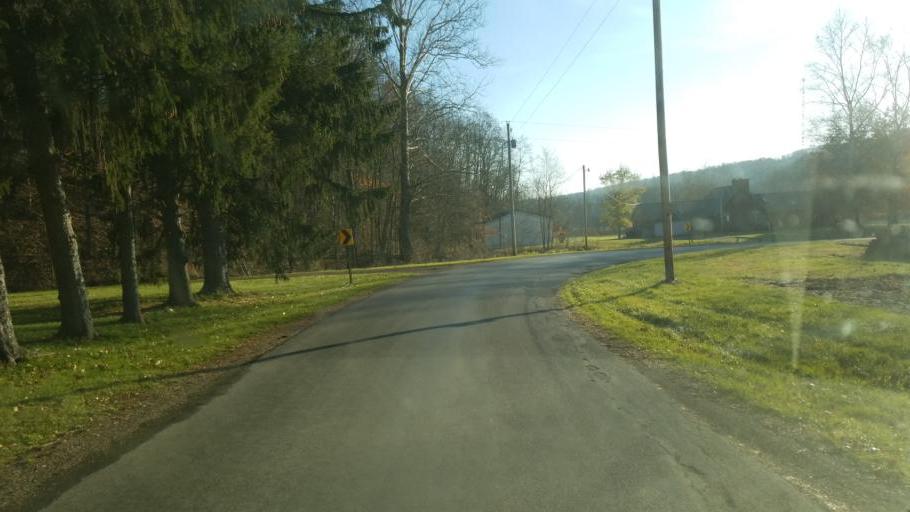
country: US
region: Ohio
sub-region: Wayne County
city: Wooster
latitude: 40.8955
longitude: -82.0082
